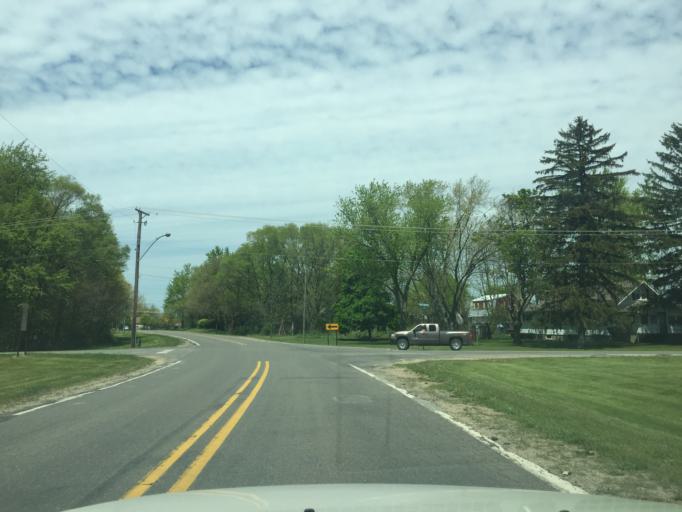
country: US
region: Michigan
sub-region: Berrien County
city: Stevensville
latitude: 41.9714
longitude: -86.4910
